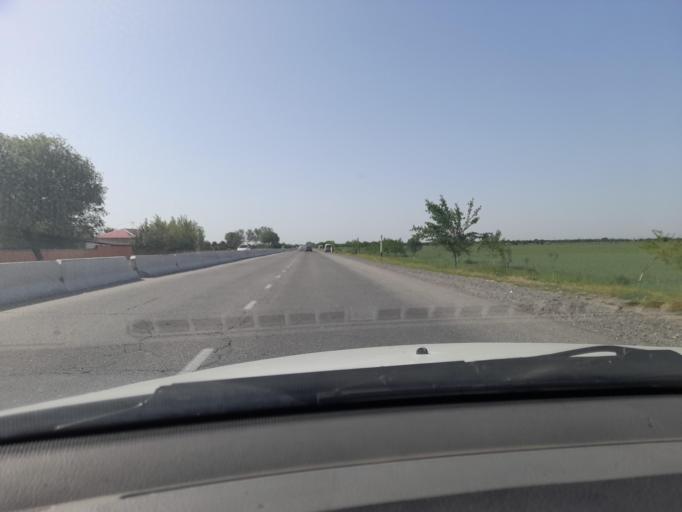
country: UZ
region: Samarqand
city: Daxbet
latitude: 39.8191
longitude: 66.8466
